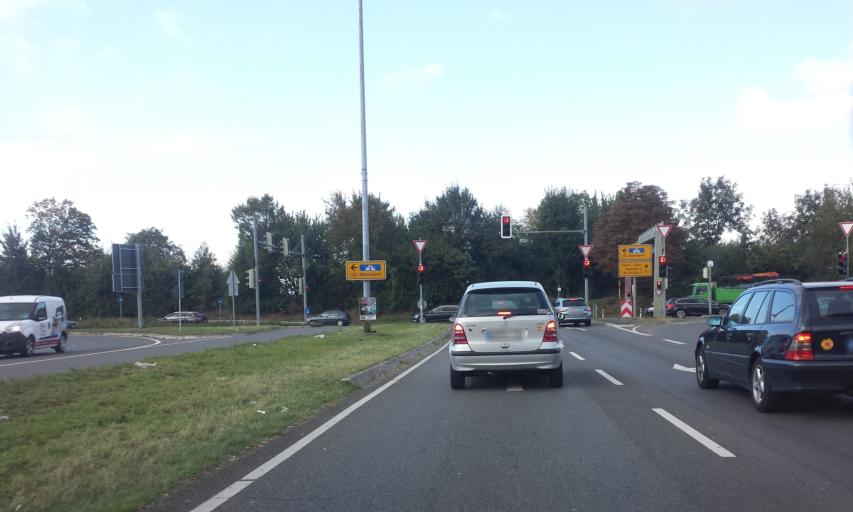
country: DE
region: Baden-Wuerttemberg
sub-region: Karlsruhe Region
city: Weinheim
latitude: 49.5495
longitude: 8.6382
